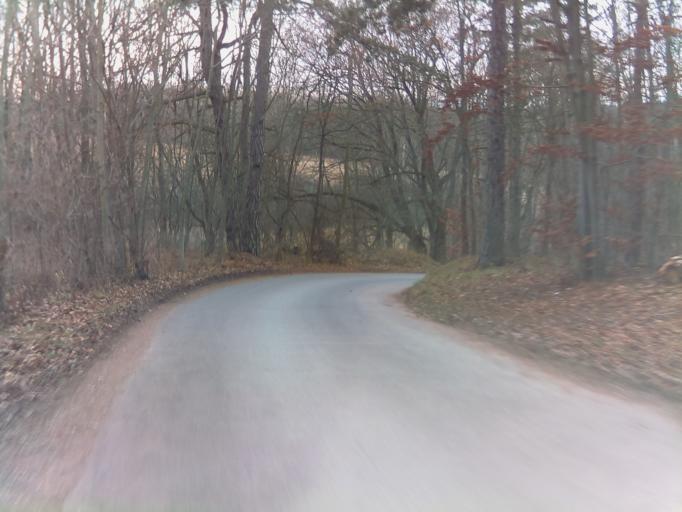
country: DE
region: Thuringia
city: Zollnitz
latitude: 50.9153
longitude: 11.6379
